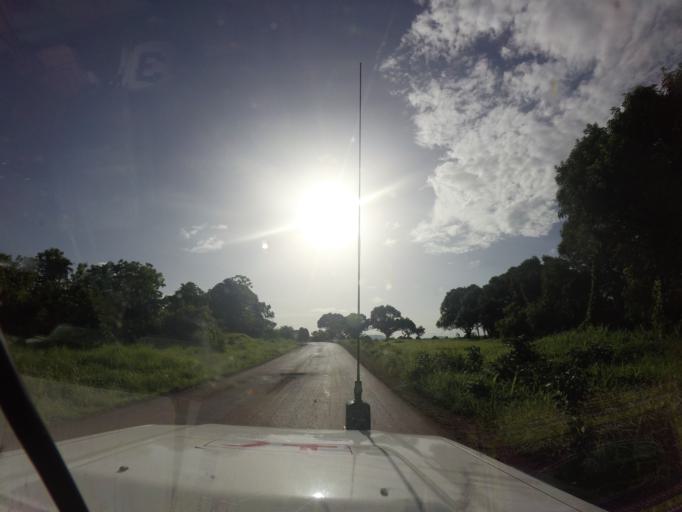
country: GN
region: Kindia
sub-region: Kindia
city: Kindia
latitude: 10.0862
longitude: -12.6390
